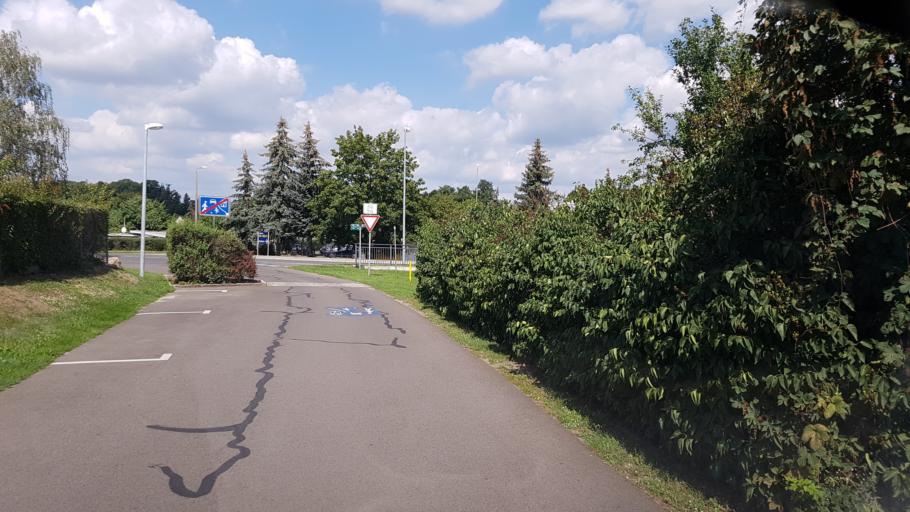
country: DE
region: Brandenburg
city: Lubbenau
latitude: 51.8642
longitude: 13.9277
